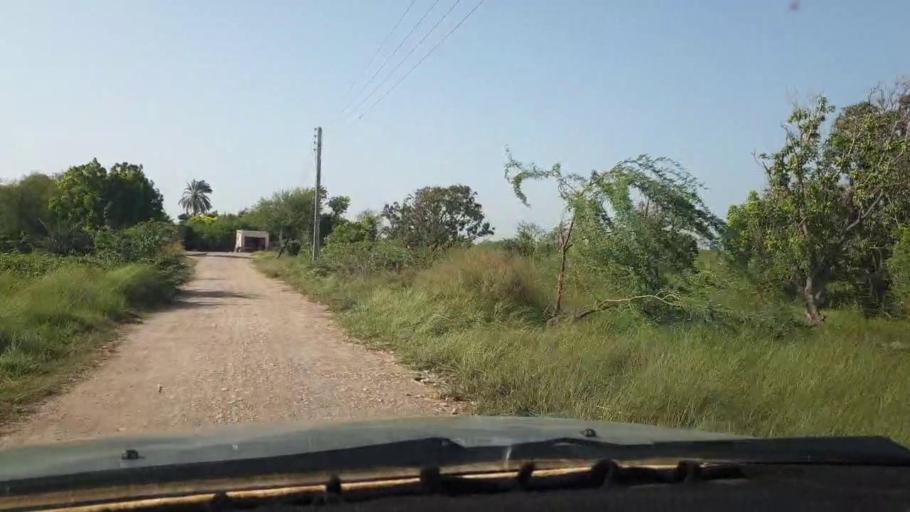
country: PK
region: Sindh
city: Chambar
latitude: 25.2701
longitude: 68.9235
